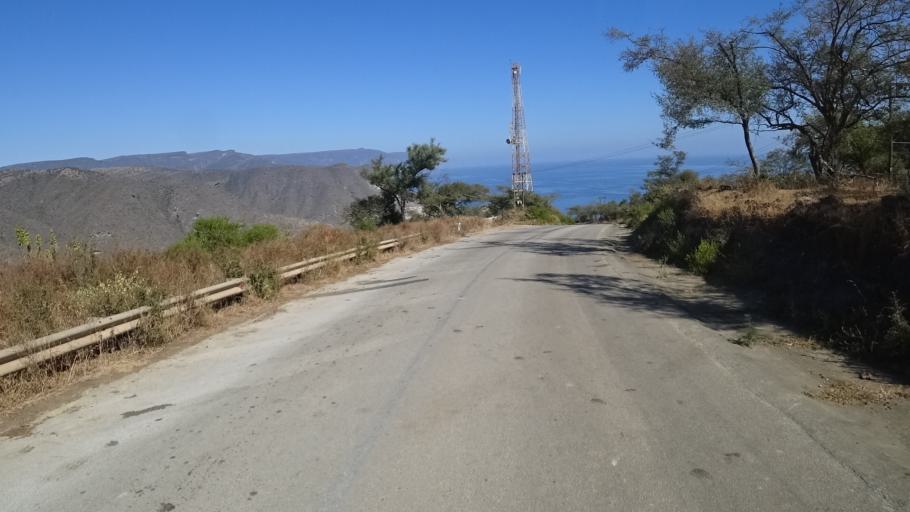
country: YE
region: Al Mahrah
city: Hawf
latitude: 16.7458
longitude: 53.3997
